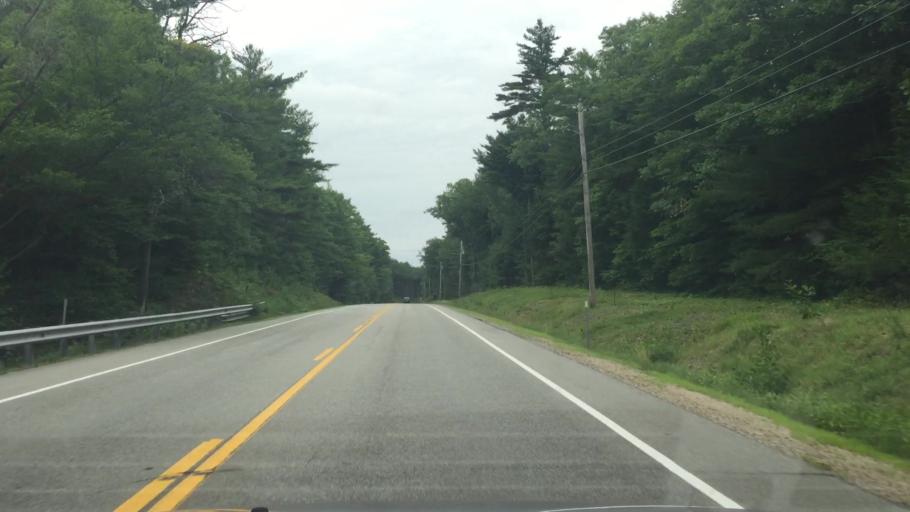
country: US
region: New Hampshire
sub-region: Carroll County
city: Sandwich
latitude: 43.7927
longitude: -71.3738
